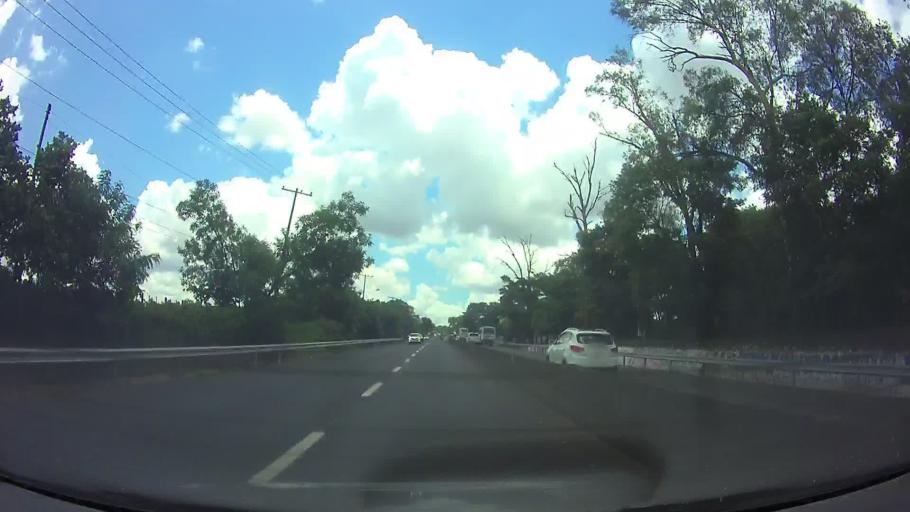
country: PY
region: Central
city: Capiata
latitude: -25.3728
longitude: -57.4121
